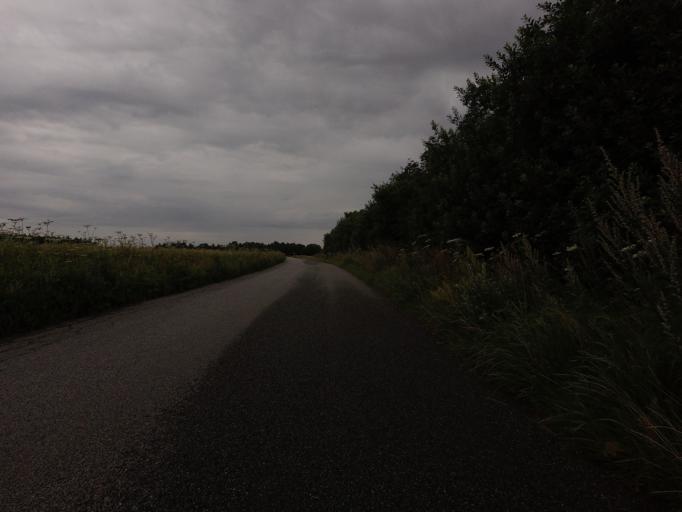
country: DK
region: North Denmark
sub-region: Alborg Kommune
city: Vadum
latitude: 57.1100
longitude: 9.8800
